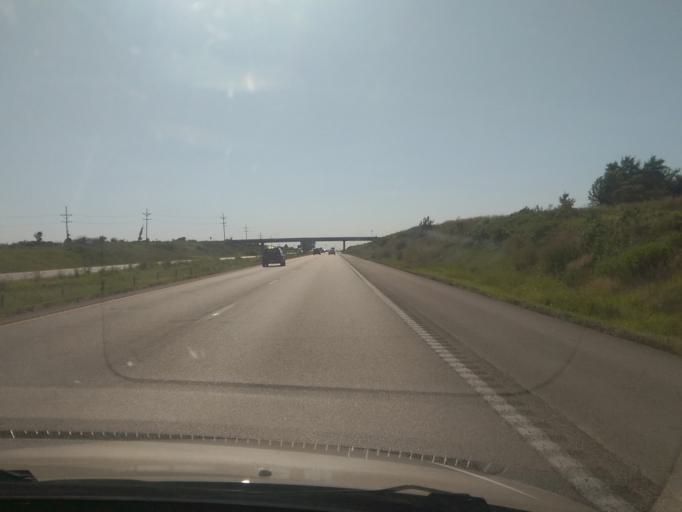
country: US
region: Missouri
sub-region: Saline County
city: Sweet Springs
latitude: 38.9786
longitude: -93.4551
